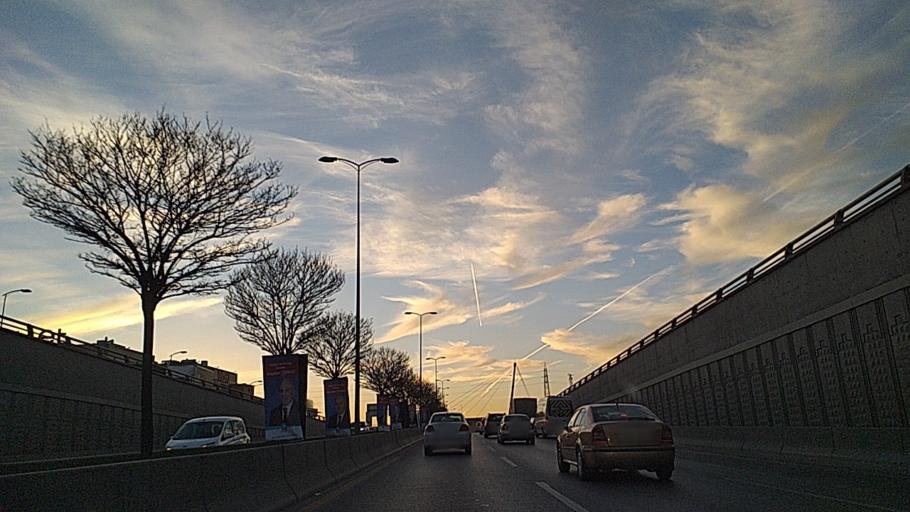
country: TR
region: Ankara
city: Etimesgut
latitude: 39.9659
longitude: 32.6349
